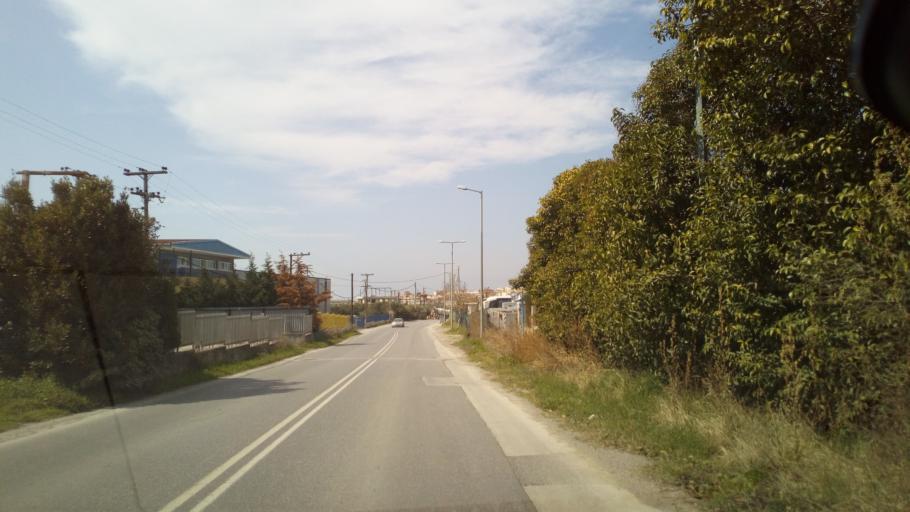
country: GR
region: Central Macedonia
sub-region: Nomos Thessalonikis
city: Thermi
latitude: 40.5446
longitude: 23.0314
